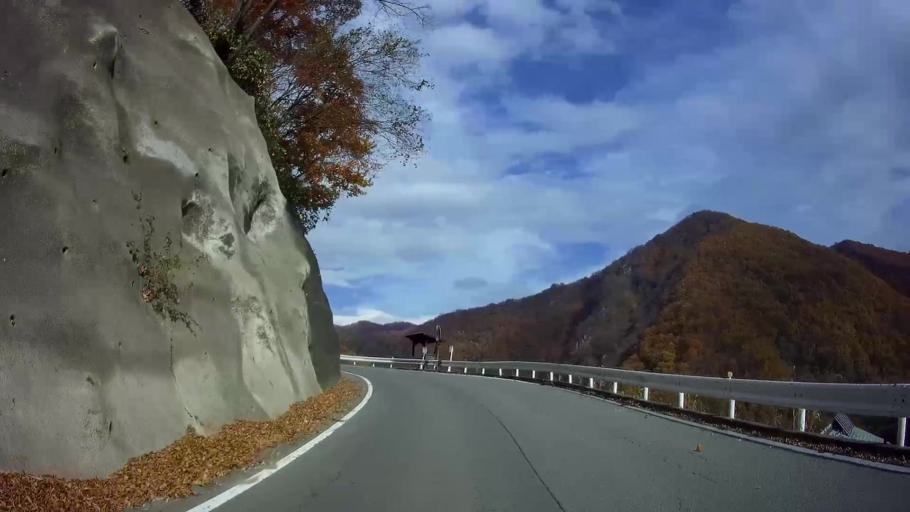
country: JP
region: Gunma
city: Nakanojomachi
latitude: 36.6163
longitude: 138.6384
